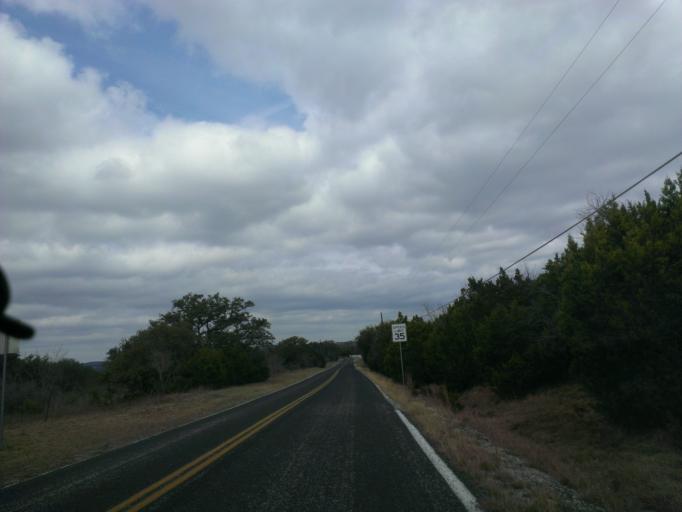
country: US
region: Texas
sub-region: Travis County
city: Briarcliff
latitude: 30.3912
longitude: -98.1041
